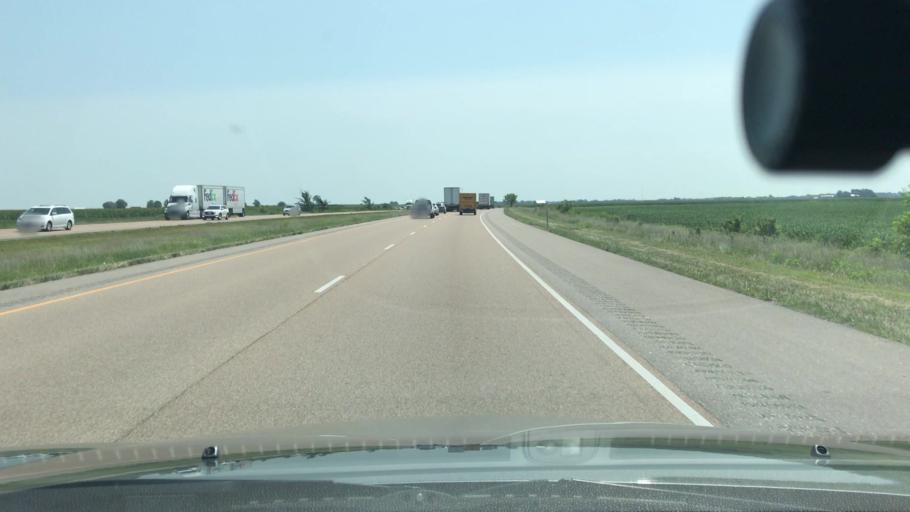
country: US
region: Illinois
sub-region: Washington County
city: Okawville
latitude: 38.4300
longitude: -89.4932
